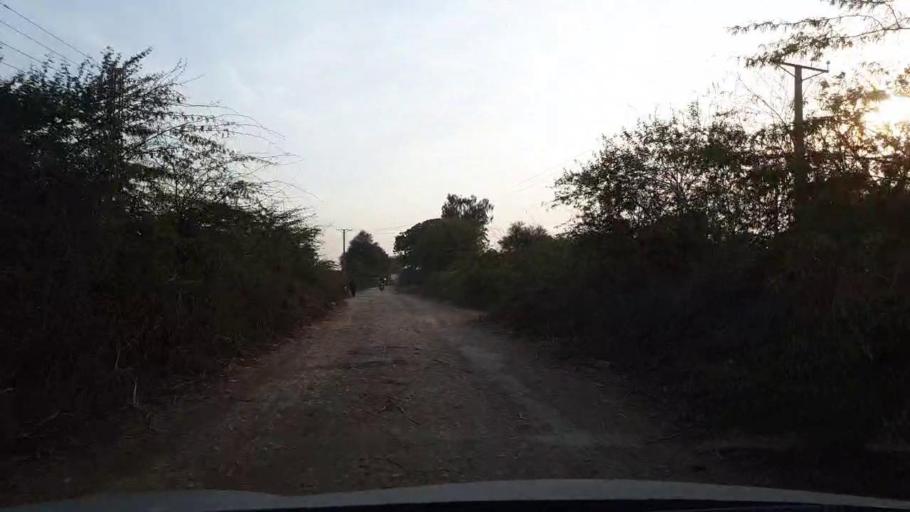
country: PK
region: Sindh
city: Tando Adam
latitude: 25.7108
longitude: 68.7201
